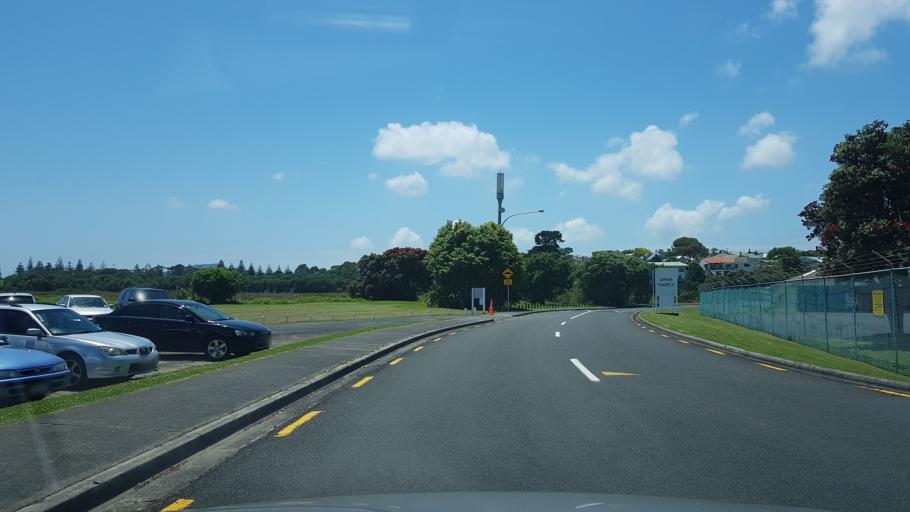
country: NZ
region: Auckland
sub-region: Auckland
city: North Shore
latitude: -36.8233
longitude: 174.7883
